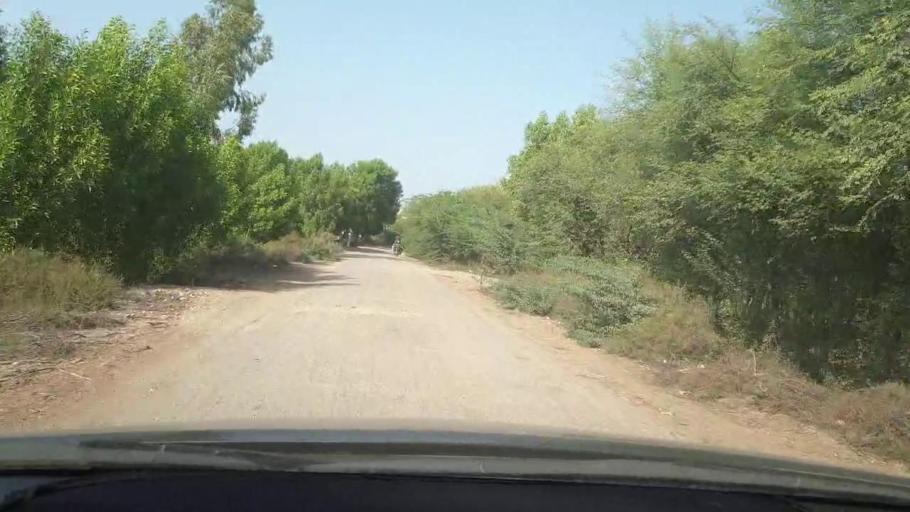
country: PK
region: Sindh
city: Naukot
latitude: 24.7670
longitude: 69.2287
